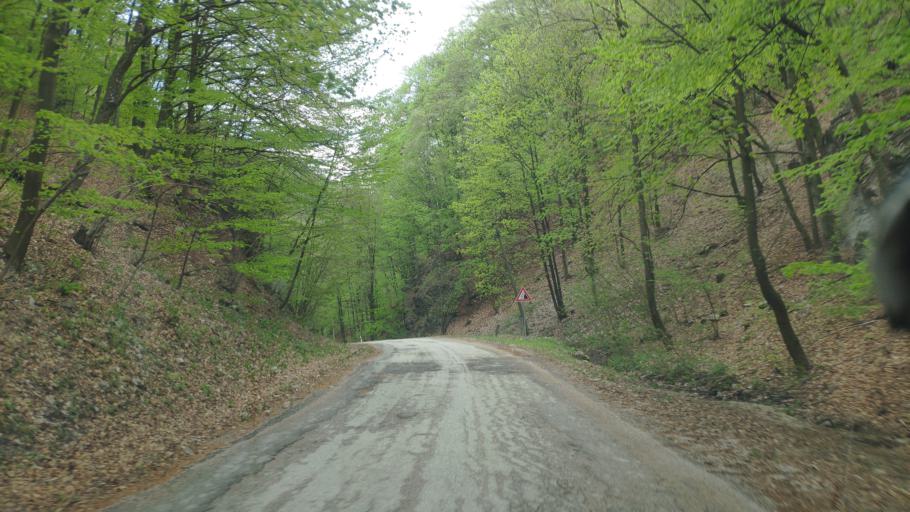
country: SK
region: Kosicky
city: Medzev
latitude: 48.6611
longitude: 20.8454
